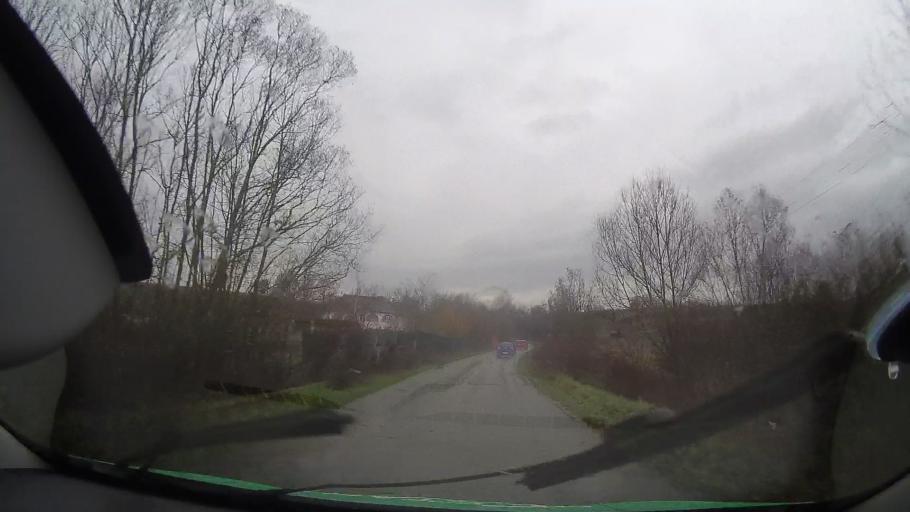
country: RO
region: Bihor
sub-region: Comuna Holod
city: Vintere
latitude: 46.7475
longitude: 22.1434
